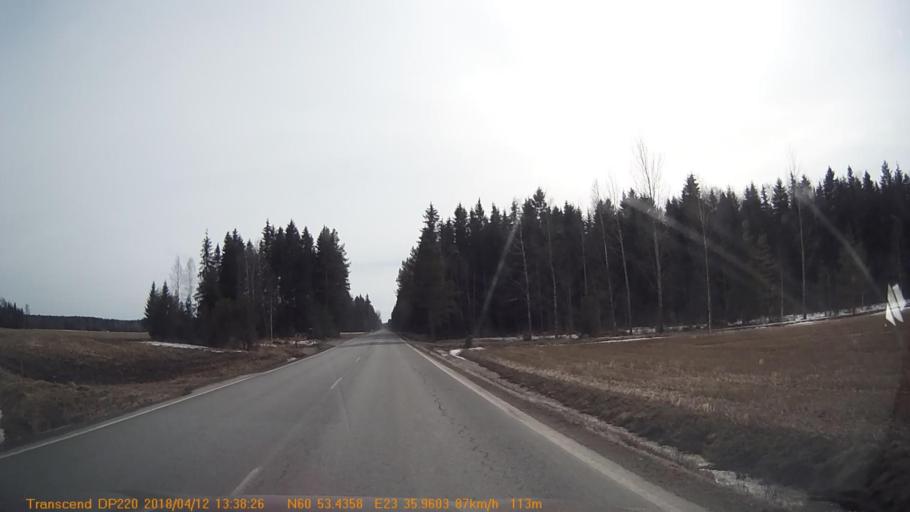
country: FI
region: Haeme
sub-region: Forssa
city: Forssa
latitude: 60.8904
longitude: 23.5994
